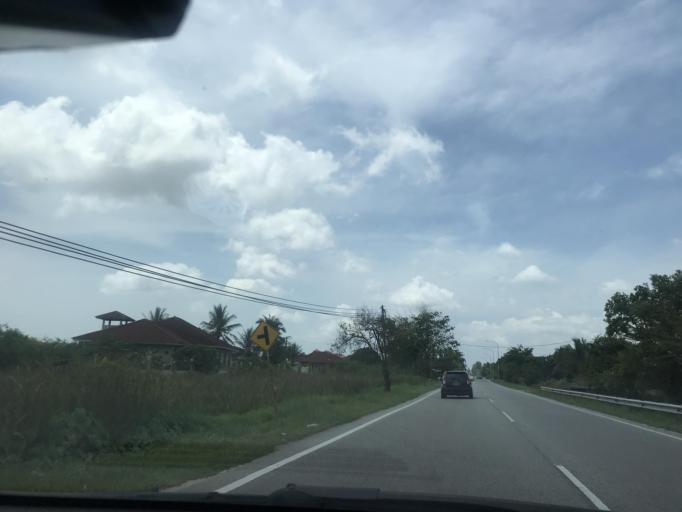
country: MY
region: Kelantan
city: Kota Bharu
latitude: 6.1501
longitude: 102.2118
